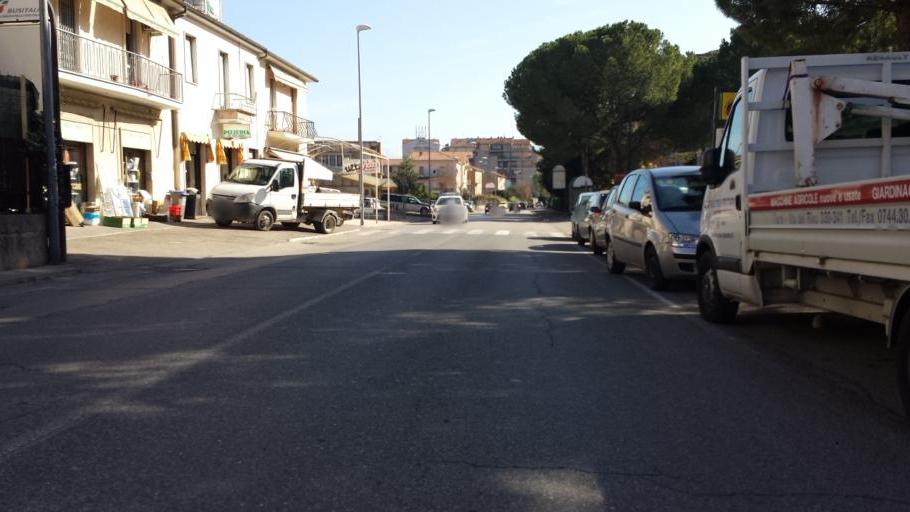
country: IT
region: Umbria
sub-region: Provincia di Terni
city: Terni
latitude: 42.5875
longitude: 12.6076
